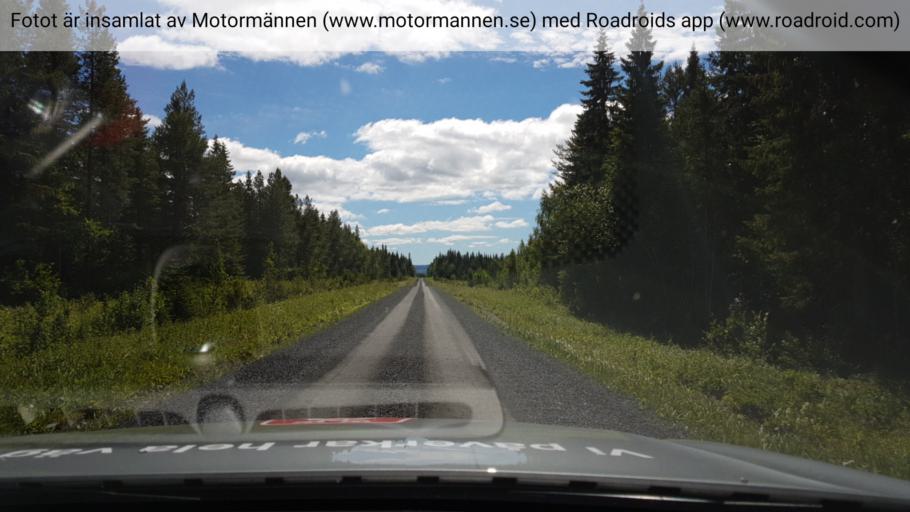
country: SE
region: Jaemtland
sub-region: Krokoms Kommun
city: Valla
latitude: 63.3452
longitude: 13.8338
